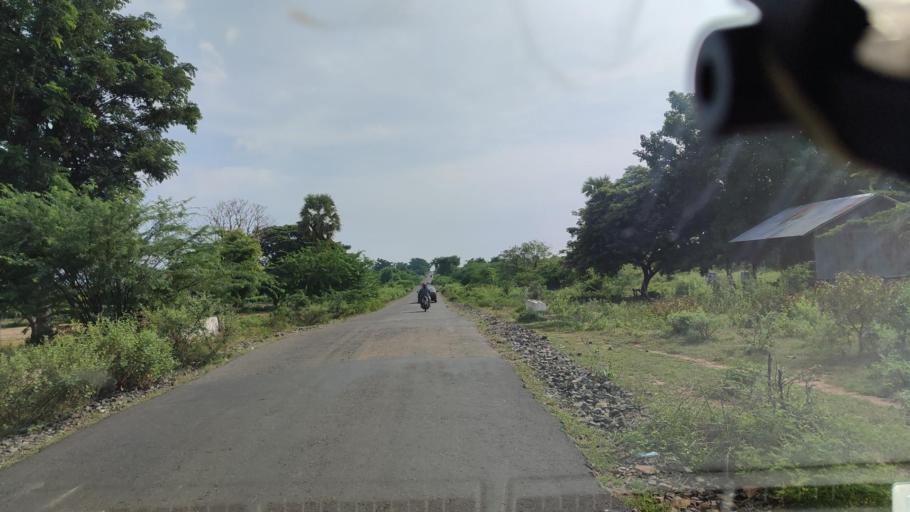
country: MM
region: Mandalay
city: Myingyan
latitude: 21.3408
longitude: 95.2826
